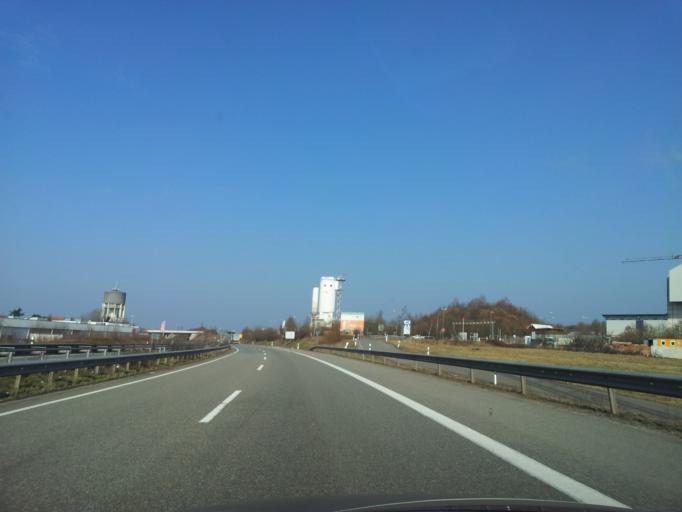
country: DE
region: Rheinland-Pfalz
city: Pirmasens
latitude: 49.2255
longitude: 7.5944
